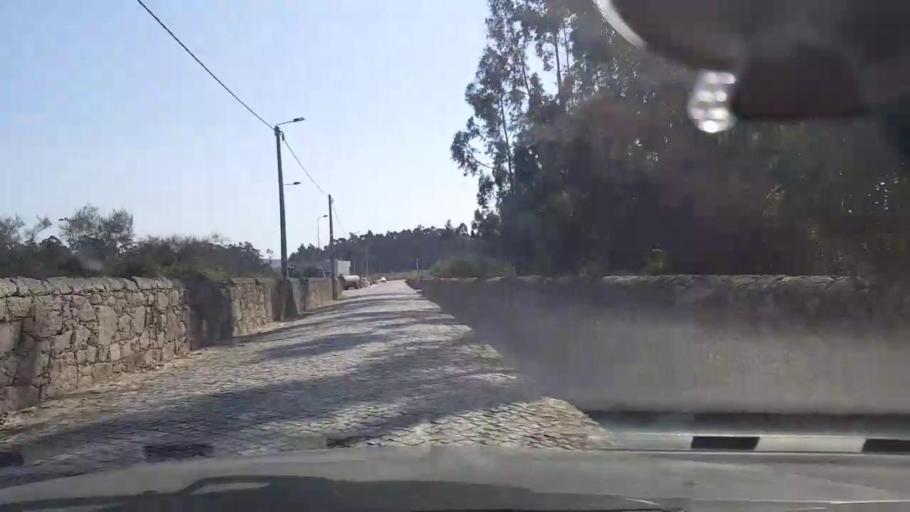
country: PT
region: Porto
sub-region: Vila do Conde
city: Vila do Conde
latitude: 41.3829
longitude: -8.7181
